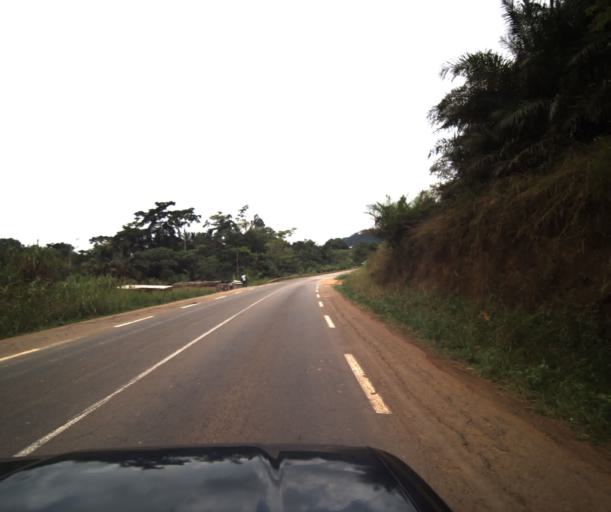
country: CM
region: Centre
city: Mbankomo
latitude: 3.7764
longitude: 11.0777
